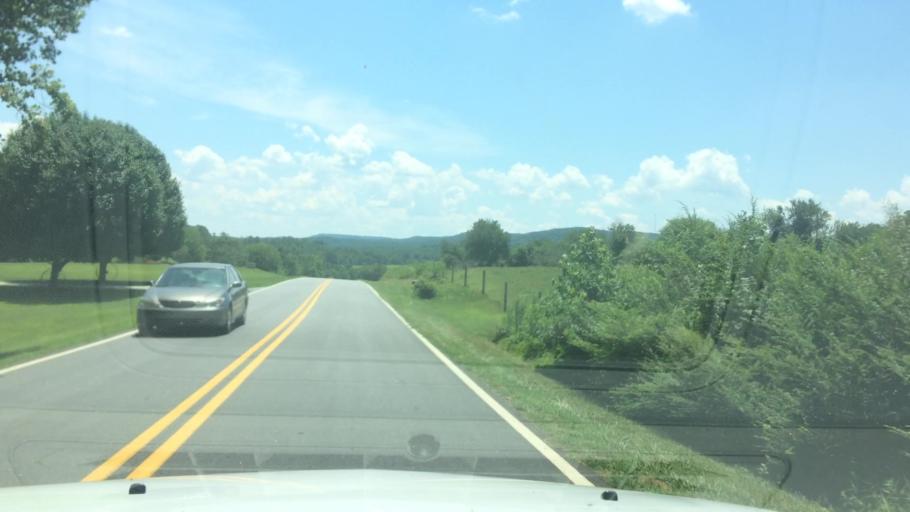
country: US
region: North Carolina
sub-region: Alexander County
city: Taylorsville
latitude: 35.9389
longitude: -81.2685
